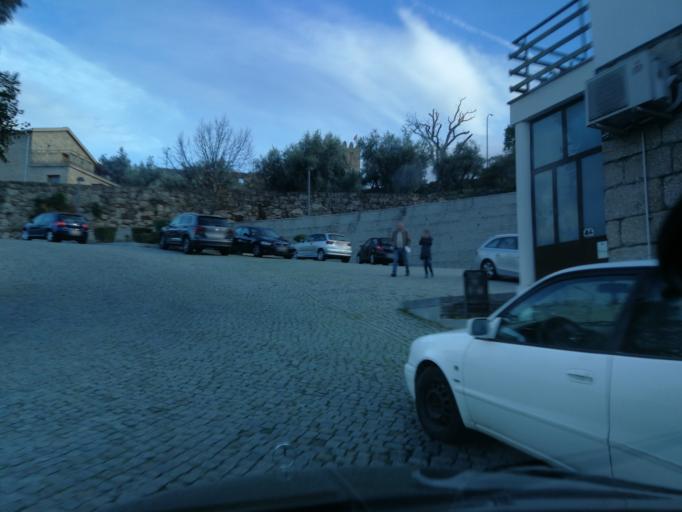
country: PT
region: Castelo Branco
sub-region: Belmonte
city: Belmonte
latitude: 40.3601
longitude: -7.3493
